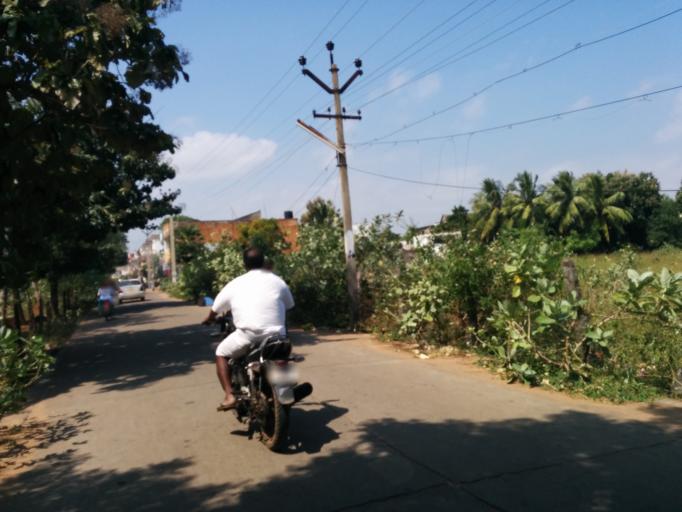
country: IN
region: Tamil Nadu
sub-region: Villupuram
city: Auroville
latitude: 11.9856
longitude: 79.8426
